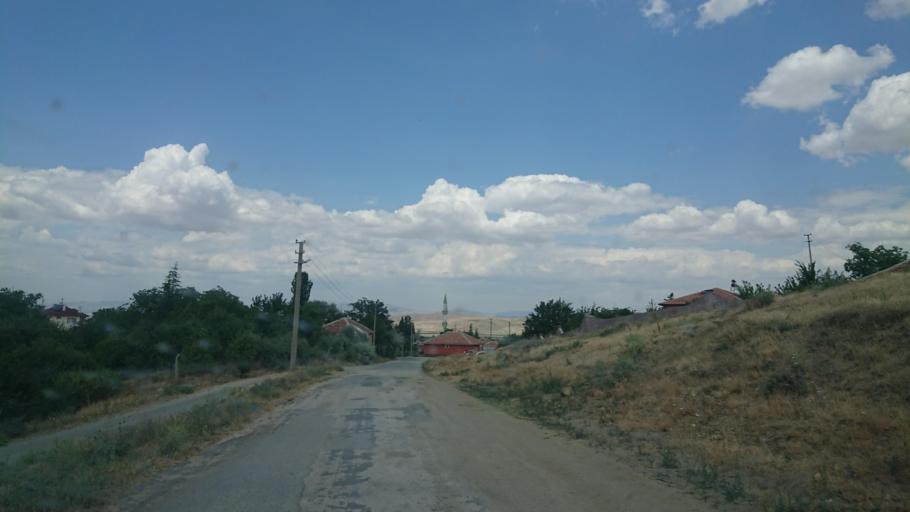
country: TR
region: Aksaray
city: Sariyahsi
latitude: 38.9573
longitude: 33.8837
